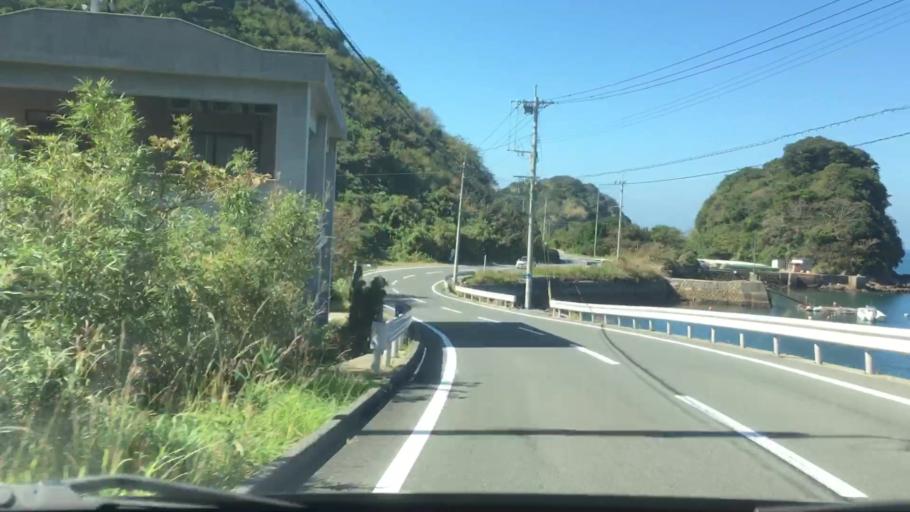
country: JP
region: Nagasaki
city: Sasebo
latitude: 33.0078
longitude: 129.5633
